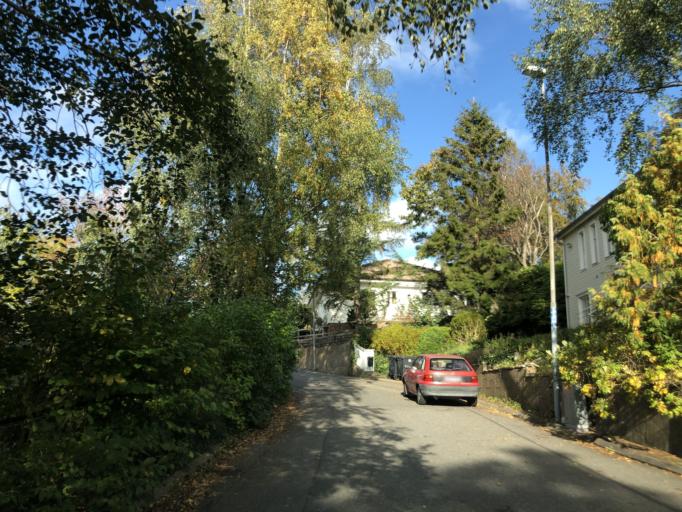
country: SE
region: Vaestra Goetaland
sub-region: Molndal
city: Moelndal
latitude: 57.6602
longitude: 12.0327
